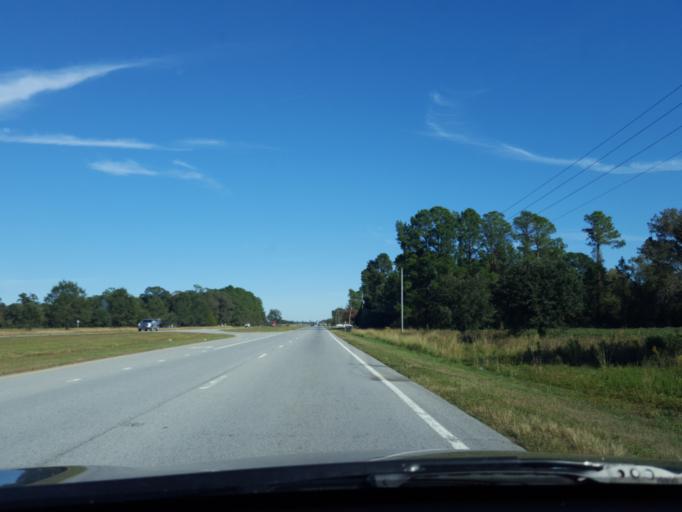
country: US
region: North Carolina
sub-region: Pitt County
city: Greenville
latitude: 35.6256
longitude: -77.2867
